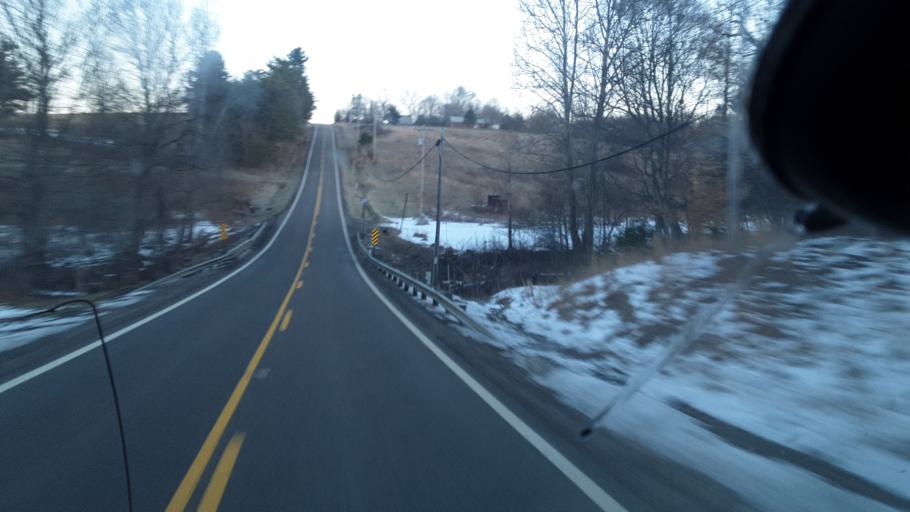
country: US
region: Ohio
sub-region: Perry County
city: Somerset
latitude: 39.7502
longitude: -82.3050
